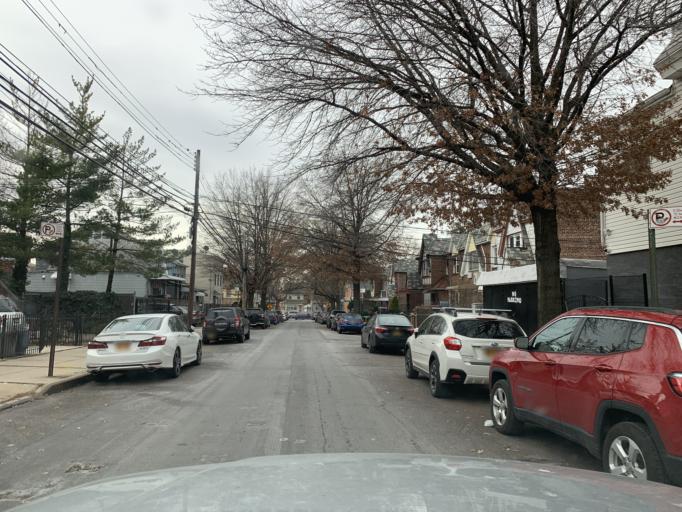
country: US
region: New York
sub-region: Queens County
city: Borough of Queens
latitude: 40.7402
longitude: -73.8745
